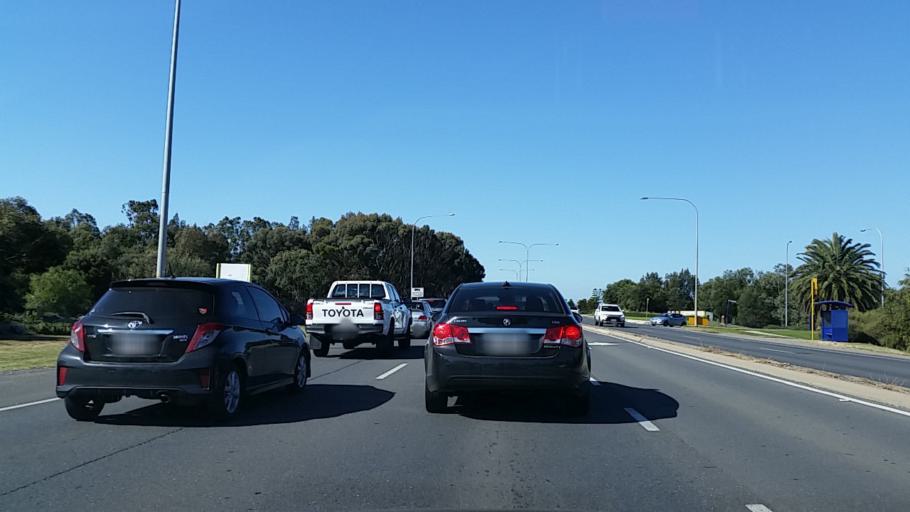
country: AU
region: South Australia
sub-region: Salisbury
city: Ingle Farm
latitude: -34.8057
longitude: 138.6026
